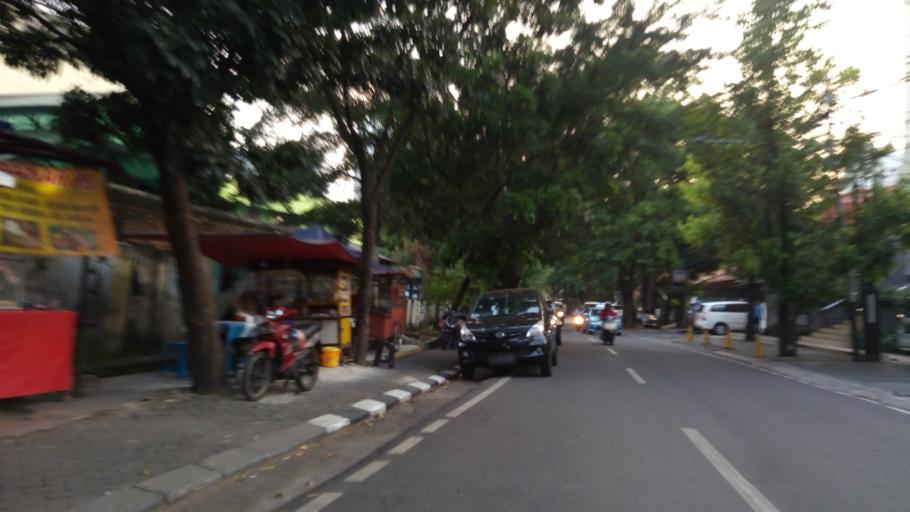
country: ID
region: Jakarta Raya
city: Jakarta
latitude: -6.2442
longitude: 106.7911
